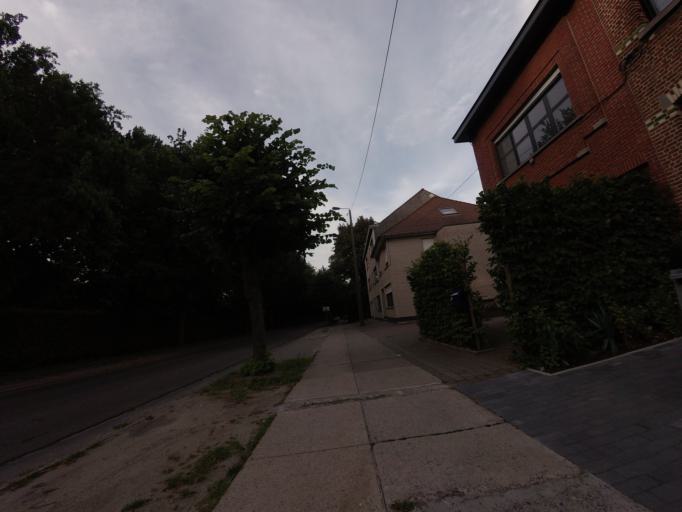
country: BE
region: Flanders
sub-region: Provincie Vlaams-Brabant
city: Grimbergen
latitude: 50.9635
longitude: 4.3713
